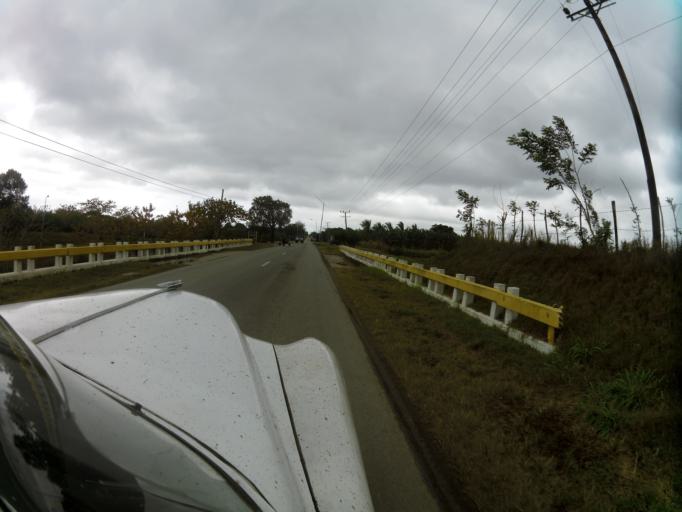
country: CU
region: Las Tunas
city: Las Tunas
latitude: 20.9353
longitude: -76.9247
